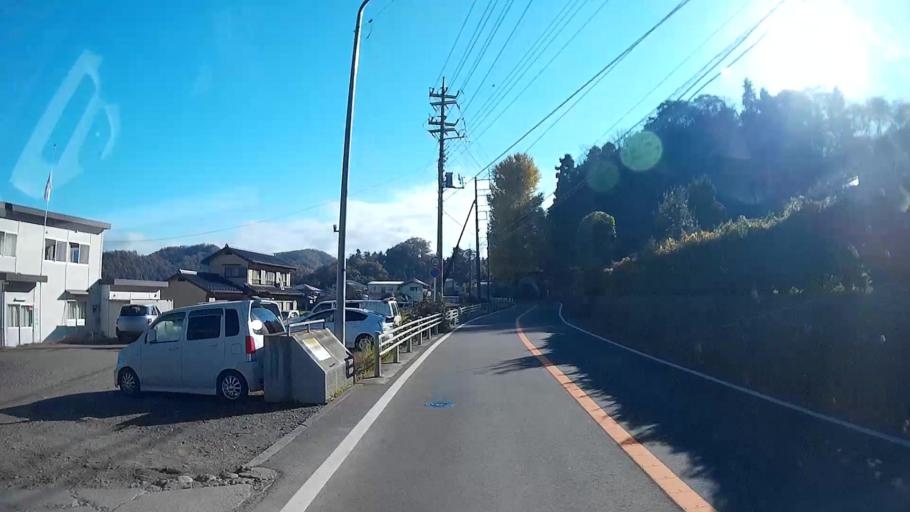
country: JP
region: Yamanashi
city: Uenohara
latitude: 35.6093
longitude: 139.1215
